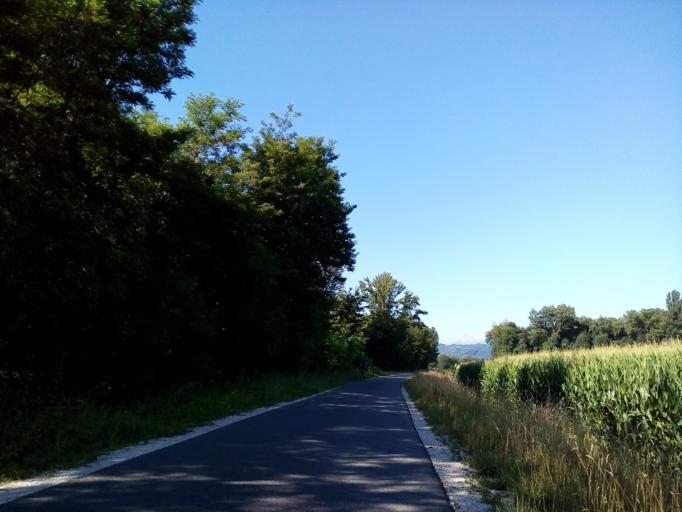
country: FR
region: Rhone-Alpes
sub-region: Departement de l'Isere
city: Domene
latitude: 45.2098
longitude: 5.8271
